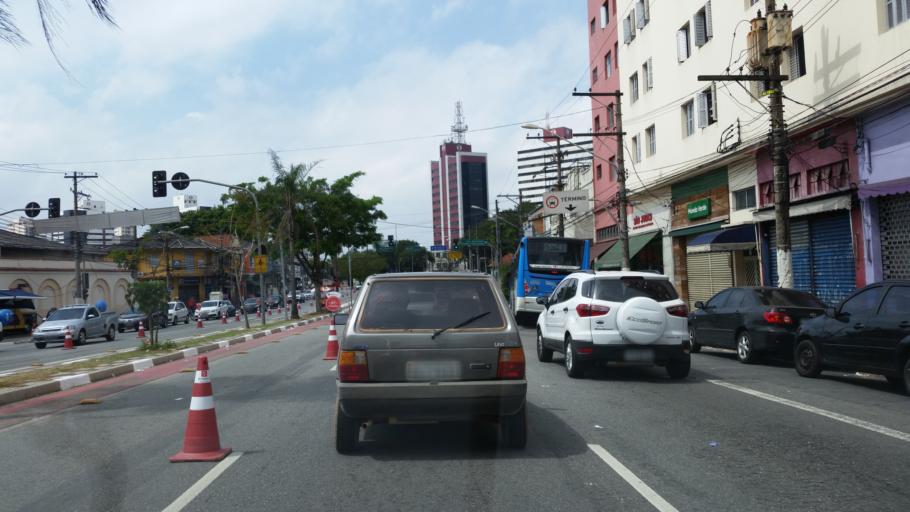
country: BR
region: Sao Paulo
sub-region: Diadema
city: Diadema
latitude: -23.6276
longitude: -46.6428
